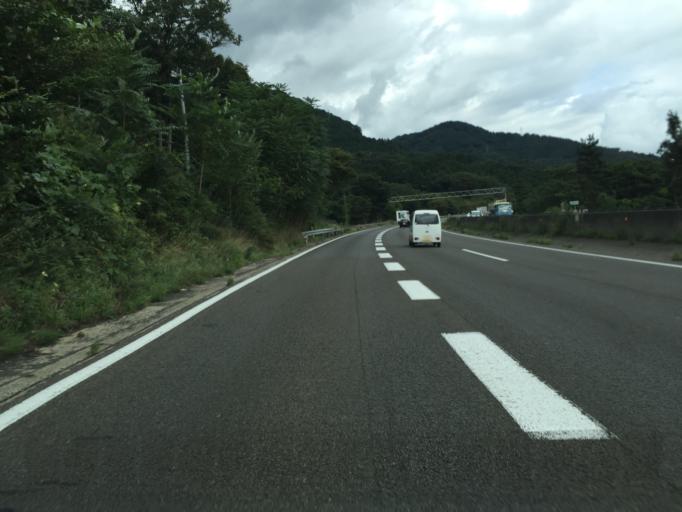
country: JP
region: Fukushima
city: Yanagawamachi-saiwaicho
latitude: 37.8991
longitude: 140.5689
